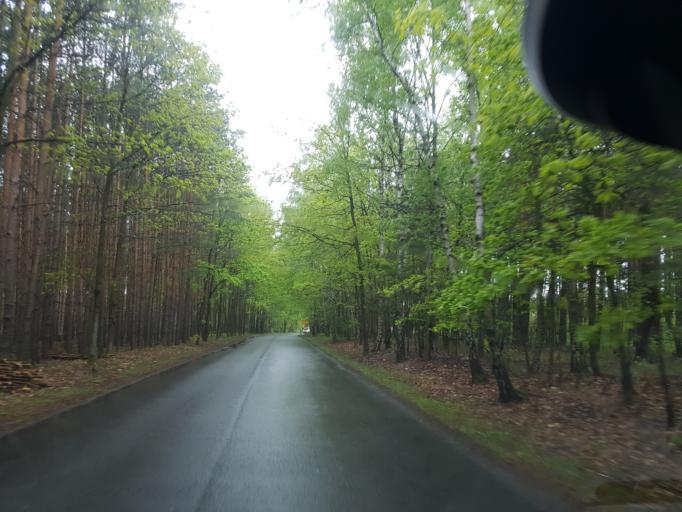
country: DE
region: Brandenburg
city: Tschernitz
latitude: 51.6306
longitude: 14.6038
